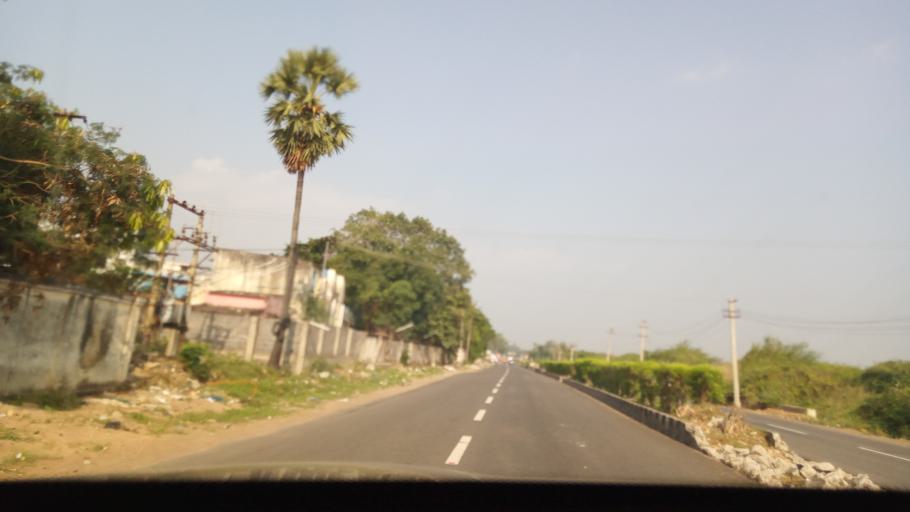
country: IN
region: Tamil Nadu
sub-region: Kancheepuram
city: Vengavasal
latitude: 12.8544
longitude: 80.1371
